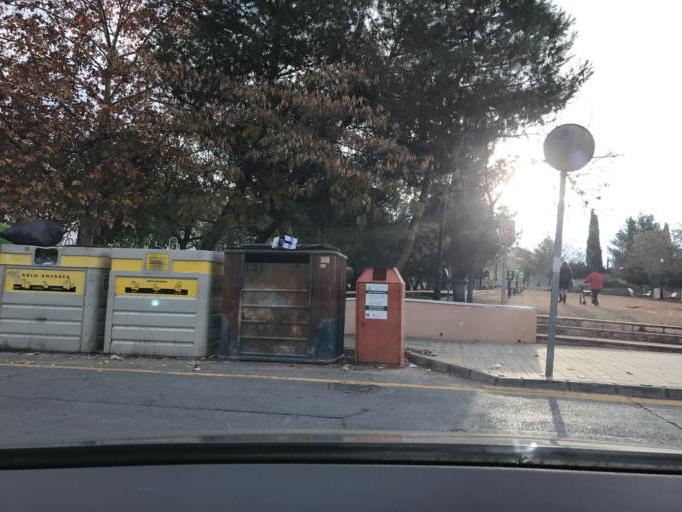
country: ES
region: Andalusia
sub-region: Provincia de Granada
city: Huetor Vega
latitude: 37.1520
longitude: -3.5720
